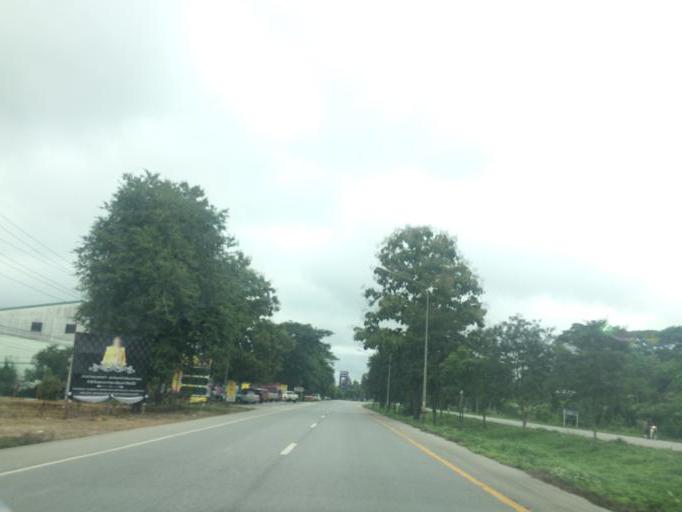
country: TH
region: Chiang Rai
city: Mae Lao
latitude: 19.8146
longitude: 99.7587
